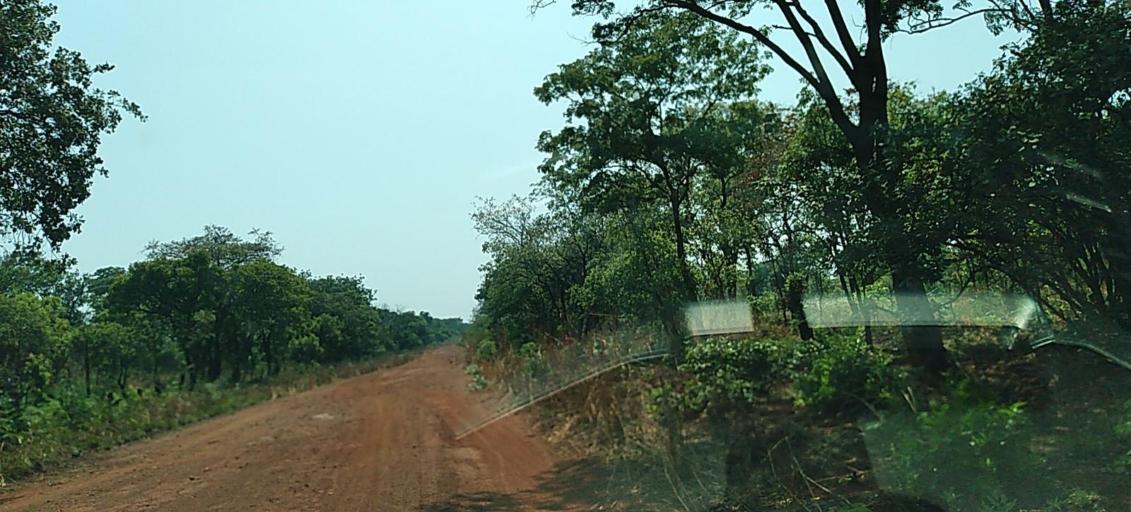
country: ZM
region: North-Western
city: Kansanshi
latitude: -12.0079
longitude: 26.5181
